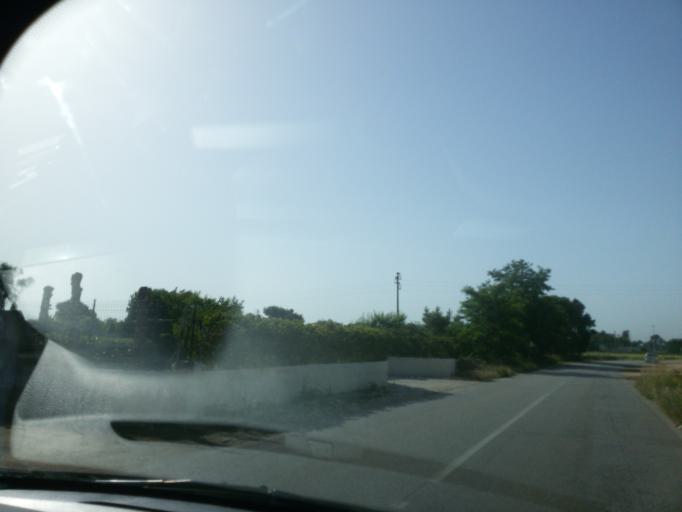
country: IT
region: Apulia
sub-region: Provincia di Brindisi
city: Mesagne
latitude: 40.5459
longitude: 17.8147
